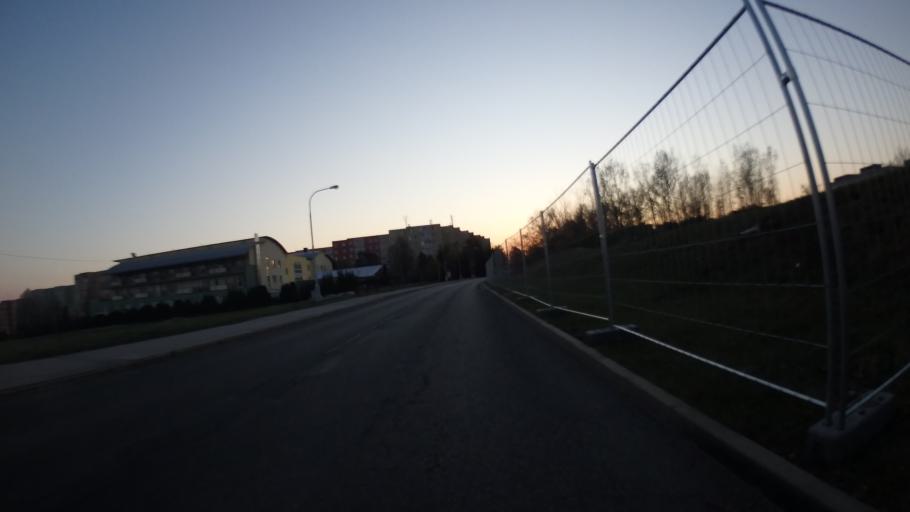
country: CZ
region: South Moravian
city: Ostopovice
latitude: 49.1714
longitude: 16.5673
